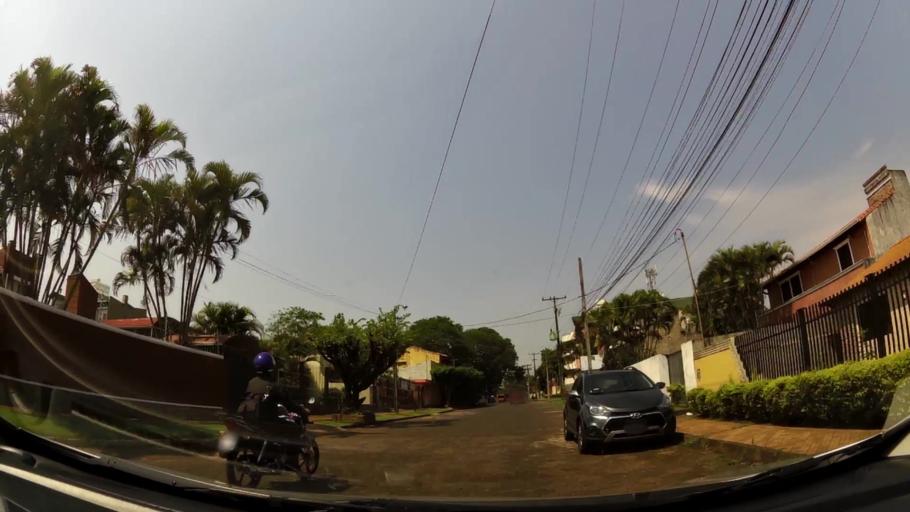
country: PY
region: Alto Parana
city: Presidente Franco
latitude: -25.5237
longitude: -54.6202
